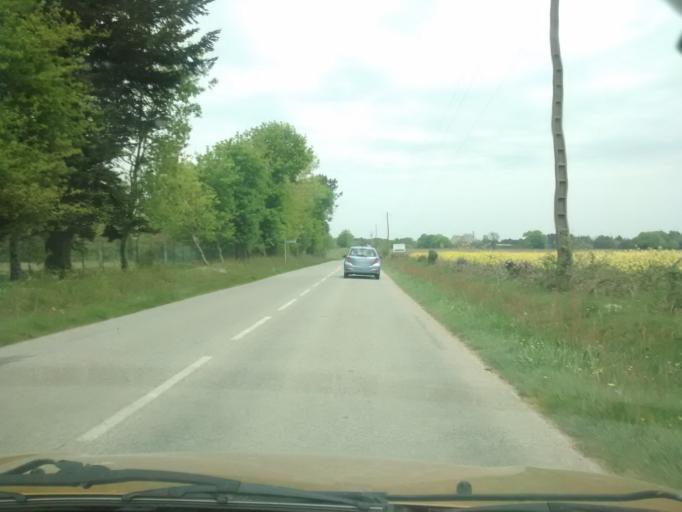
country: FR
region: Brittany
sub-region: Departement du Morbihan
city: Questembert
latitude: 47.6567
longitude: -2.4796
